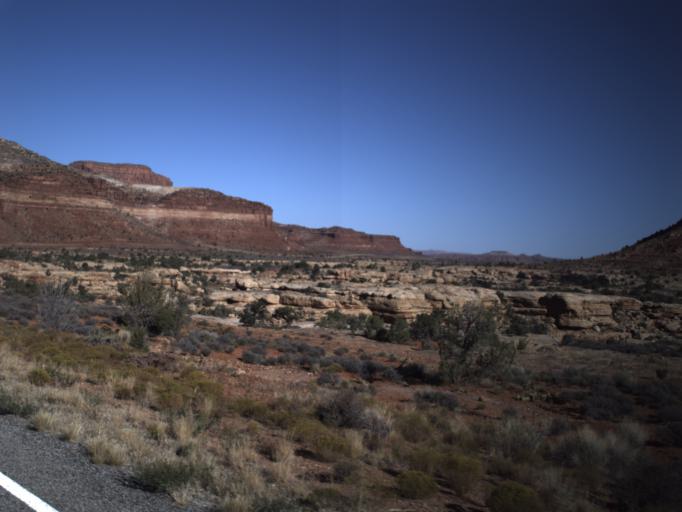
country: US
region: Utah
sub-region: San Juan County
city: Blanding
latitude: 37.7356
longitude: -110.2682
